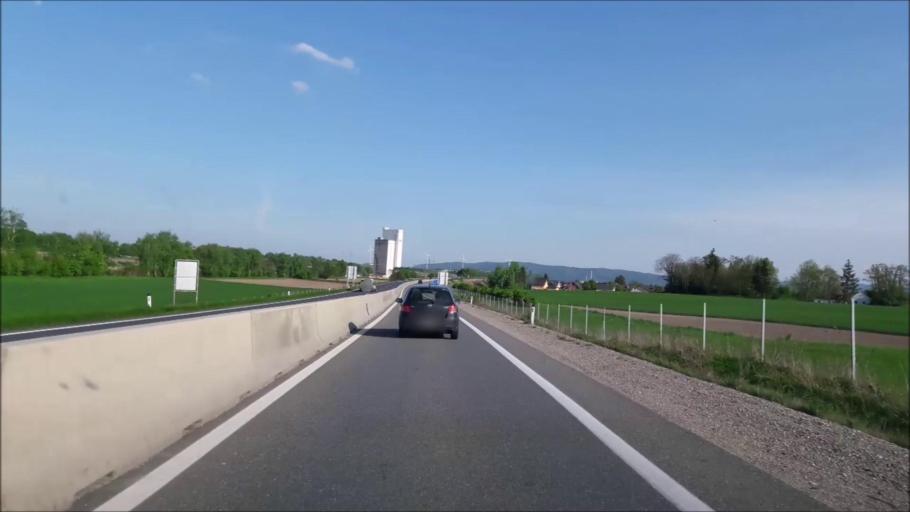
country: AT
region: Lower Austria
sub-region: Politischer Bezirk Korneuburg
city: Sierndorf
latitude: 48.4176
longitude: 16.1631
